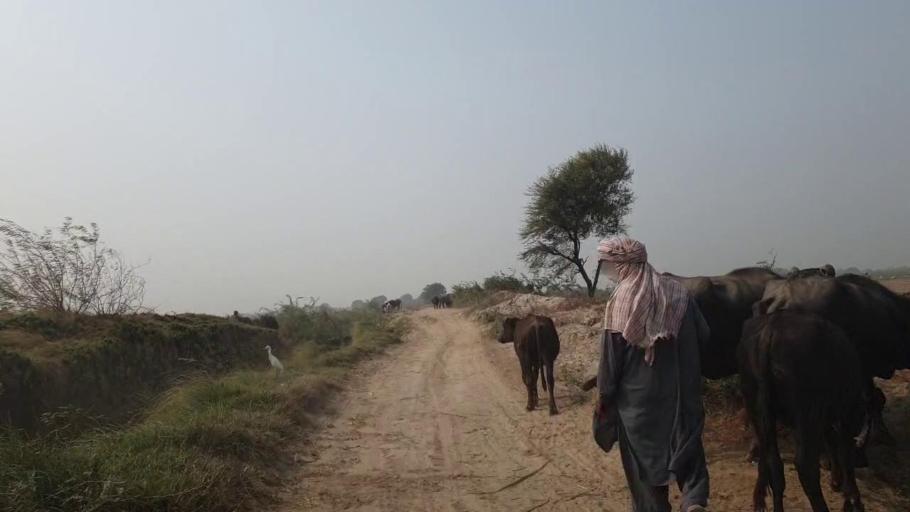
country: PK
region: Sindh
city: Tando Muhammad Khan
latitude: 25.1912
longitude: 68.5818
